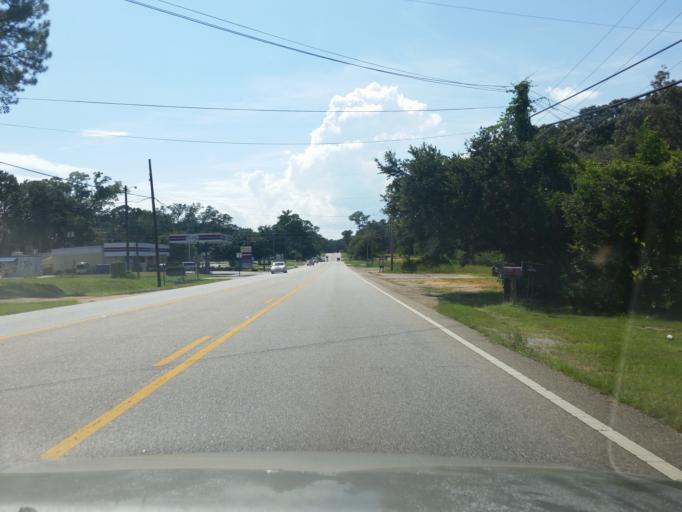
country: US
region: Alabama
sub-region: Baldwin County
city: Spanish Fort
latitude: 30.6721
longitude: -87.8815
